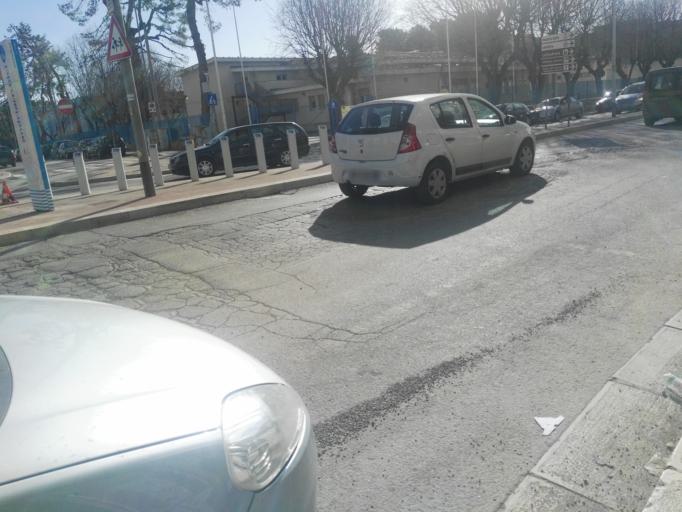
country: IT
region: Apulia
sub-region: Provincia di Barletta - Andria - Trani
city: Andria
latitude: 41.2255
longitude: 16.3072
